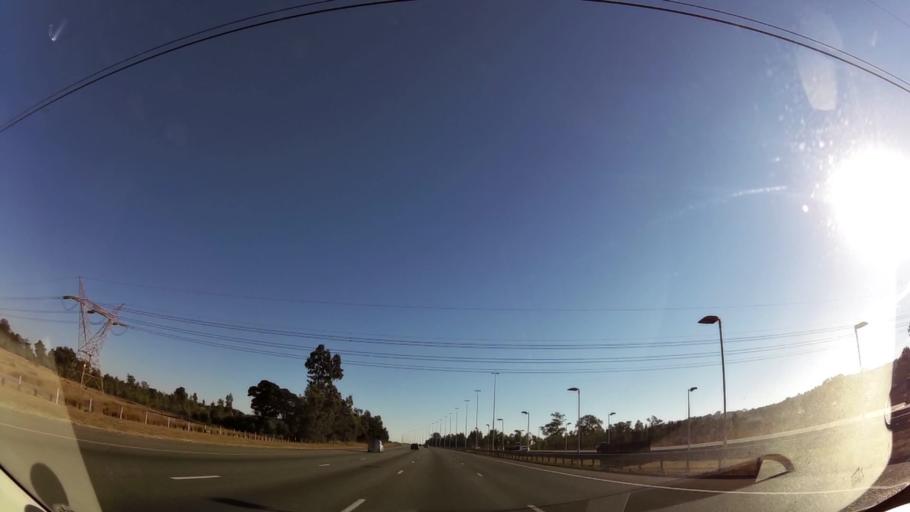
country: ZA
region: Gauteng
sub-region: Ekurhuleni Metropolitan Municipality
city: Tembisa
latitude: -25.9175
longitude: 28.2604
